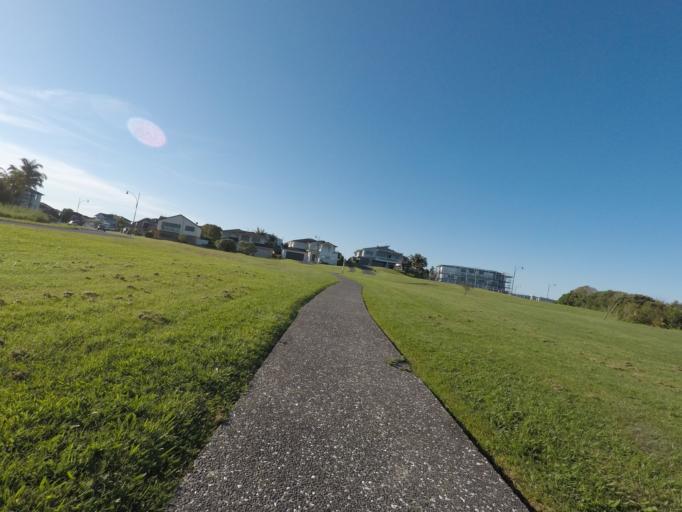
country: NZ
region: Auckland
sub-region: Auckland
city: Rosebank
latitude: -36.8369
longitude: 174.6613
